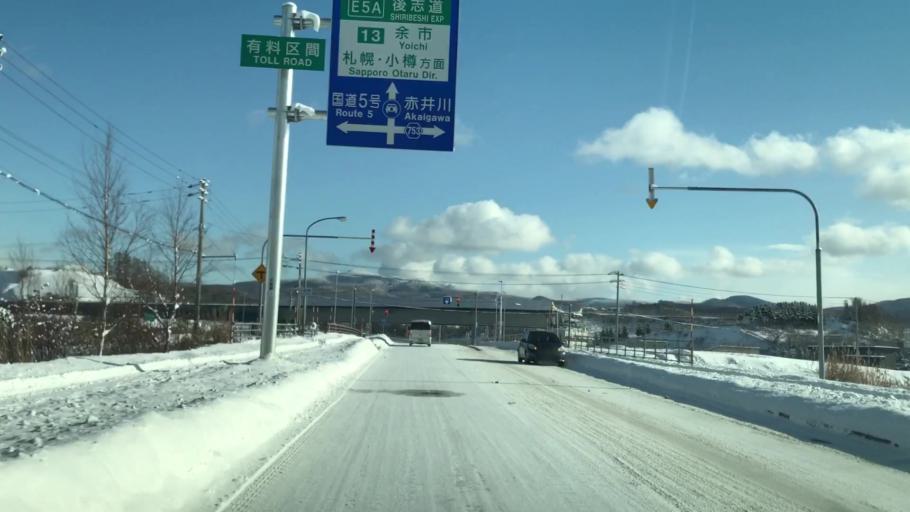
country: JP
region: Hokkaido
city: Yoichi
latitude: 43.1819
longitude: 140.8200
